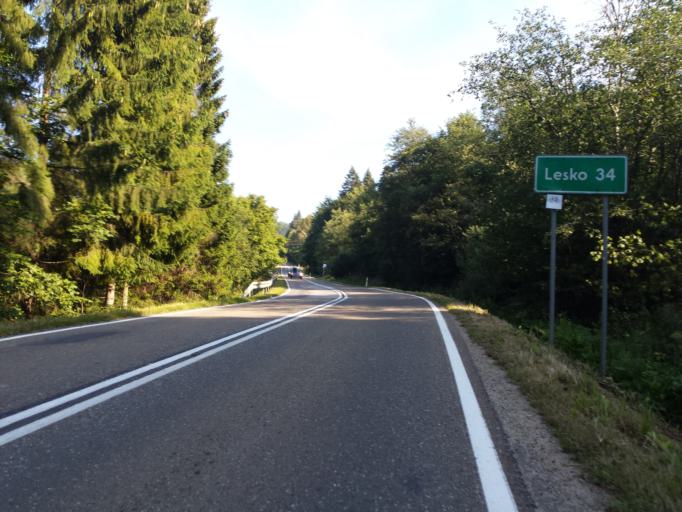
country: PL
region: Subcarpathian Voivodeship
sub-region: Powiat leski
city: Cisna
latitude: 49.2299
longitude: 22.3032
